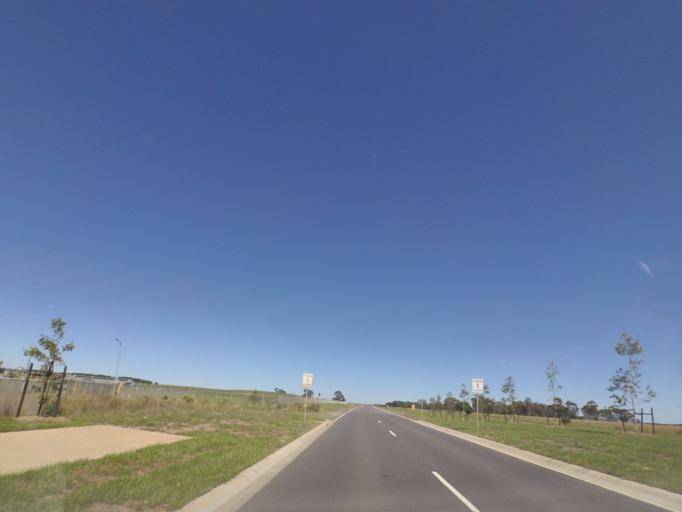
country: AU
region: Victoria
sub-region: Hume
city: Craigieburn
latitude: -37.5389
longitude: 144.9334
